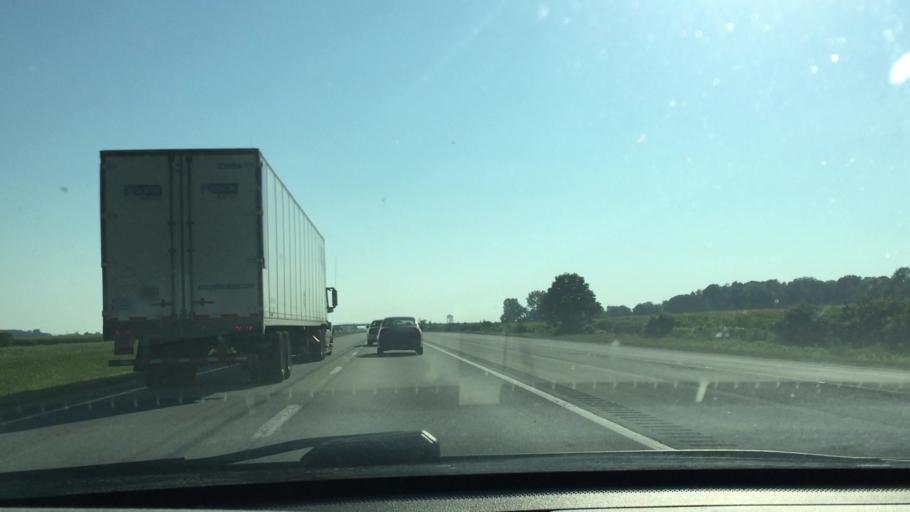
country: US
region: Ohio
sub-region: Clinton County
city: Wilmington
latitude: 39.5326
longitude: -83.7982
